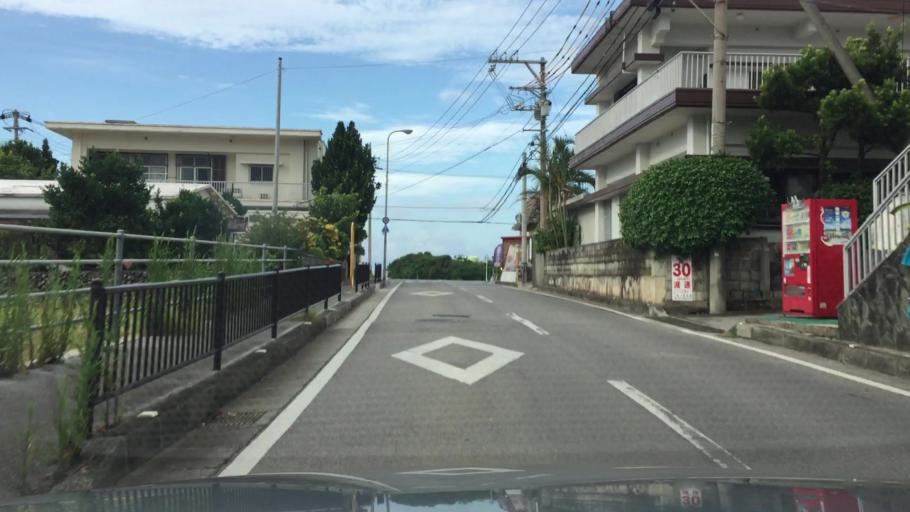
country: JP
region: Okinawa
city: Ishigaki
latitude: 24.4609
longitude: 124.1418
